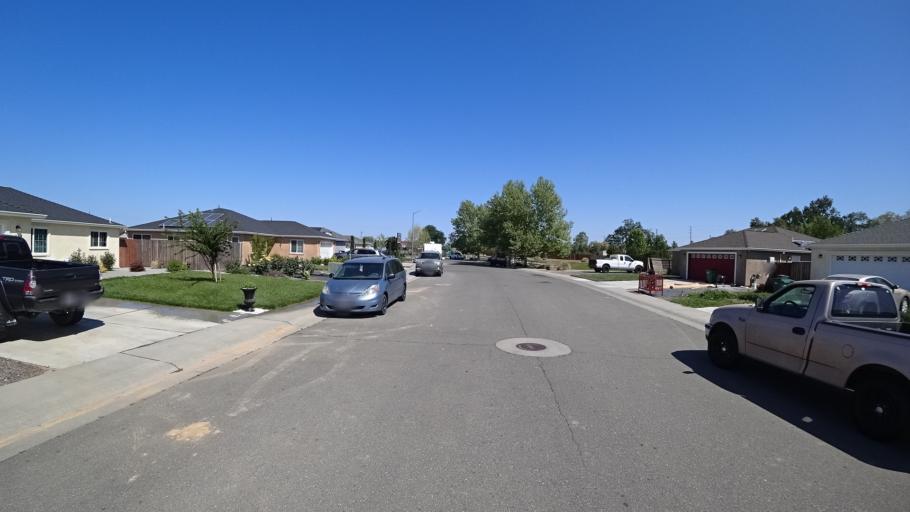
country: US
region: California
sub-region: Glenn County
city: Orland
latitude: 39.7604
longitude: -122.1988
